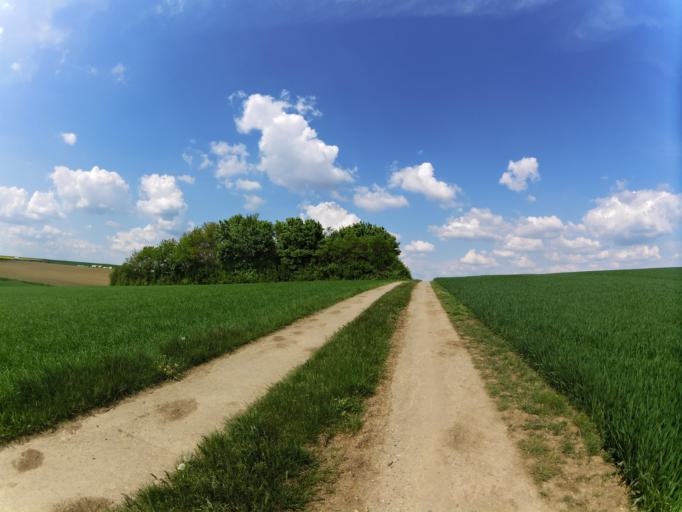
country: DE
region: Bavaria
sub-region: Regierungsbezirk Unterfranken
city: Sulzdorf
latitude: 49.6249
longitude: 9.9172
